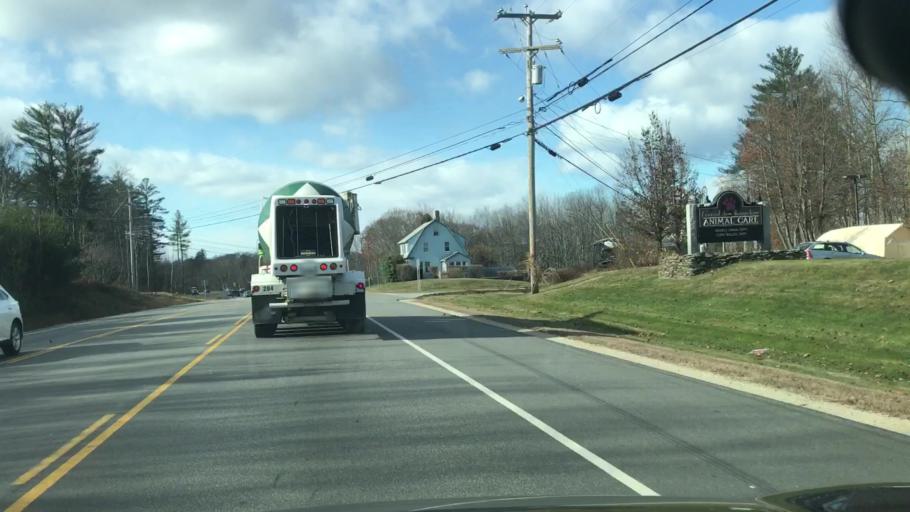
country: US
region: New Hampshire
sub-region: Merrimack County
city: Chichester
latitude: 43.2480
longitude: -71.4150
